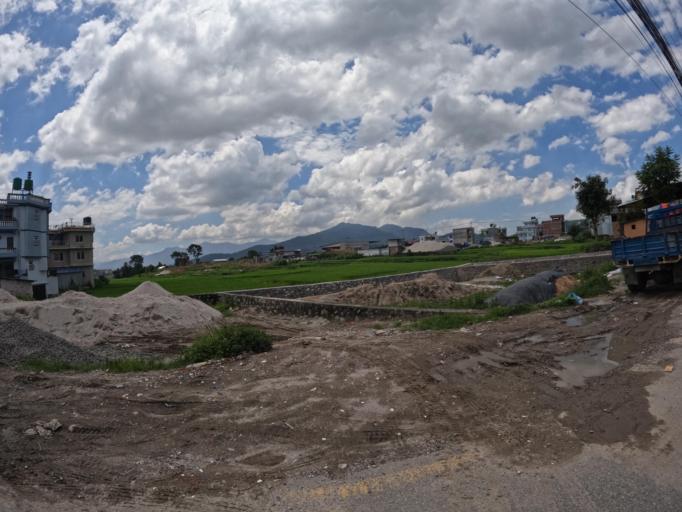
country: NP
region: Central Region
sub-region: Bagmati Zone
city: Kathmandu
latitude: 27.7769
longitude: 85.3270
